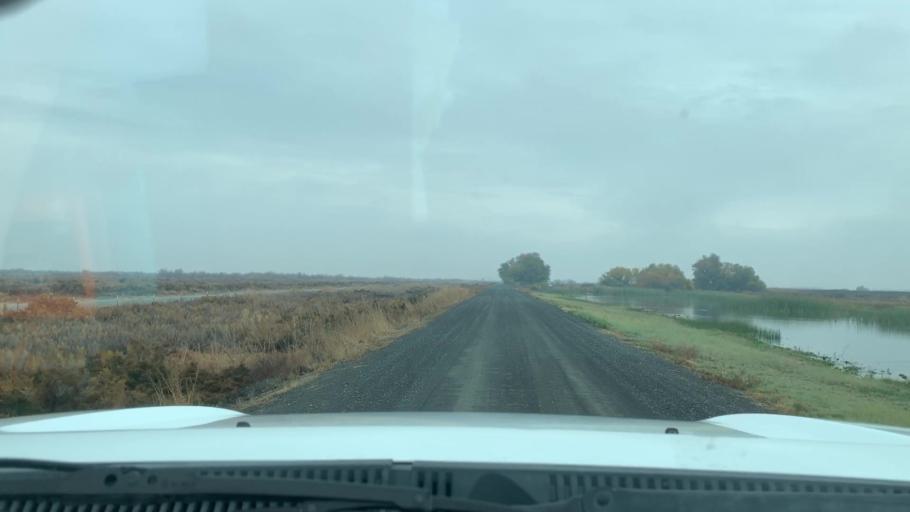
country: US
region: California
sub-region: Kern County
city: Lost Hills
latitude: 35.7359
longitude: -119.5799
